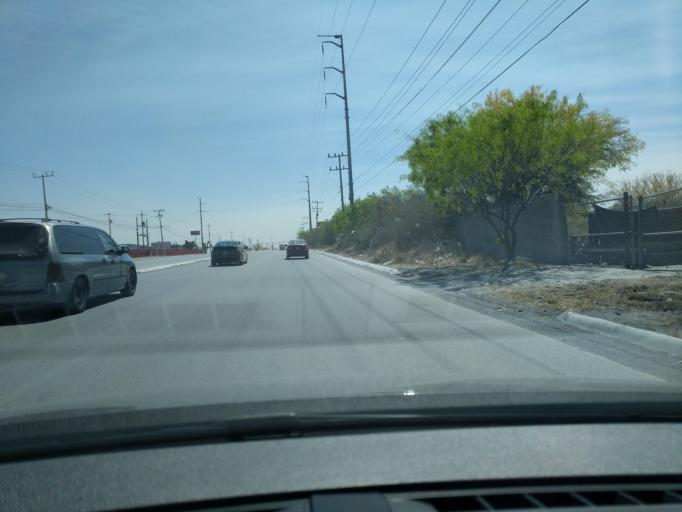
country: MX
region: Nuevo Leon
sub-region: Salinas Victoria
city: Emiliano Zapata
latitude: 25.8951
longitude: -100.2606
